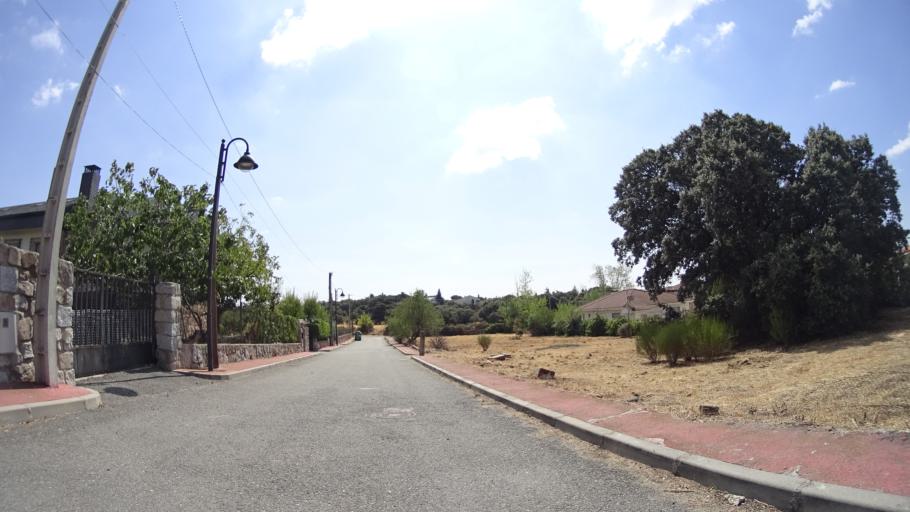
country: ES
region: Madrid
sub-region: Provincia de Madrid
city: Galapagar
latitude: 40.5931
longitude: -3.9931
